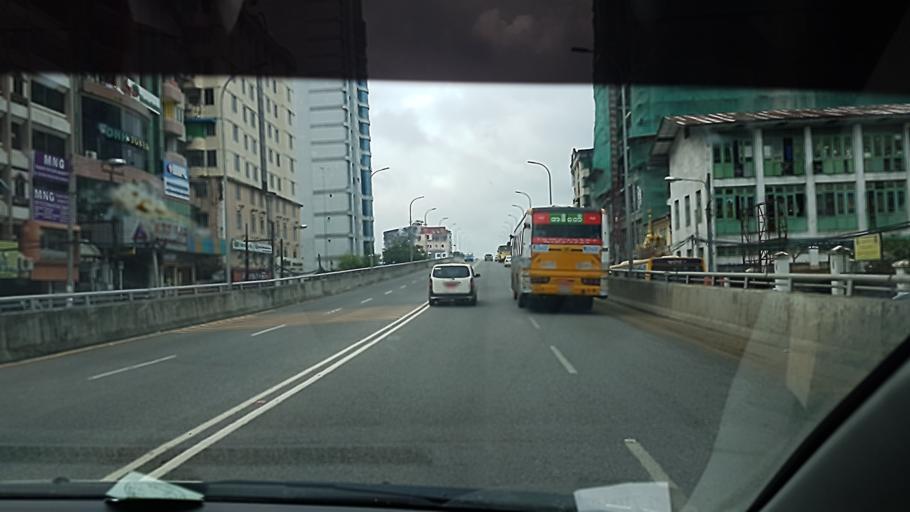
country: MM
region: Yangon
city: Yangon
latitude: 16.8057
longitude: 96.1368
